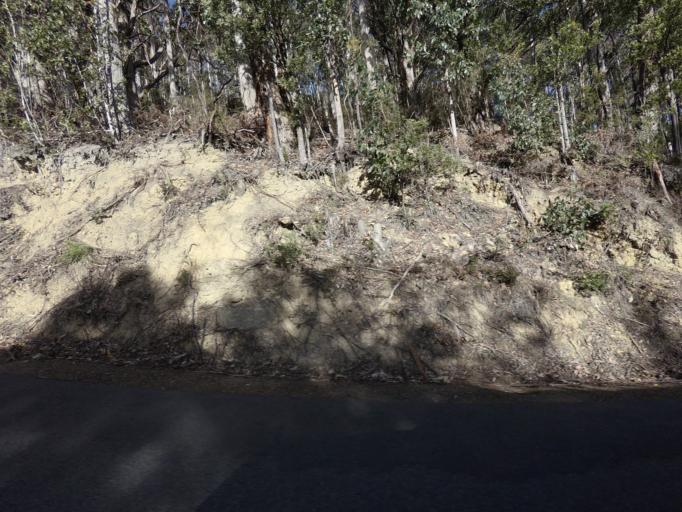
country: AU
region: Tasmania
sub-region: Kingborough
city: Kettering
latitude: -43.1696
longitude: 147.1809
